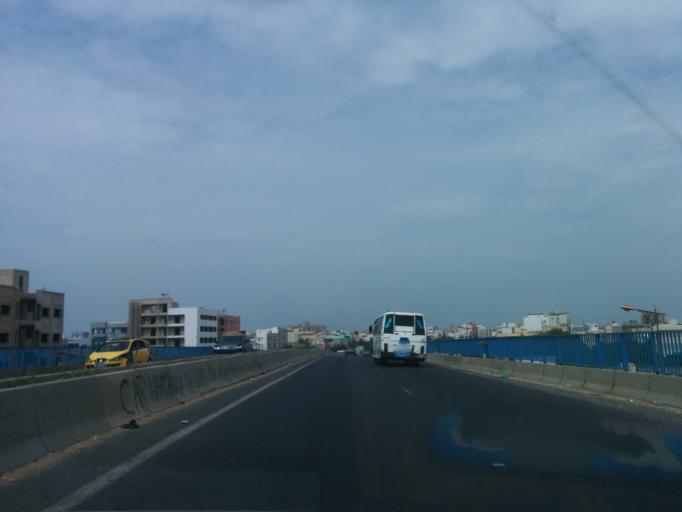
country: SN
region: Dakar
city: Grand Dakar
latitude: 14.7411
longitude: -17.4712
